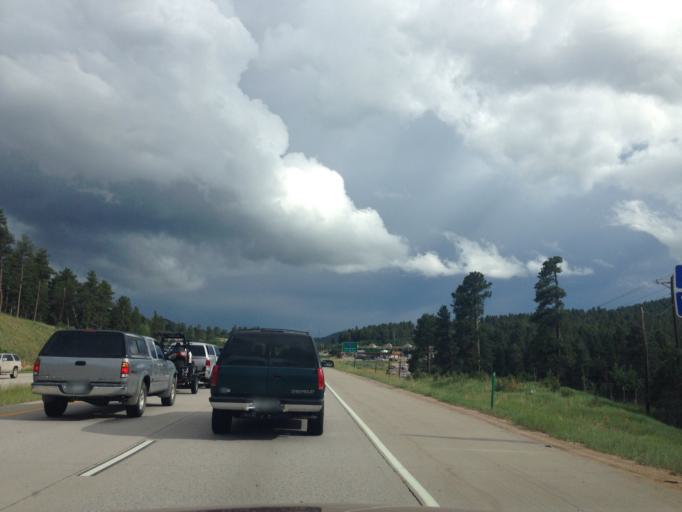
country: US
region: Colorado
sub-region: Jefferson County
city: Evergreen
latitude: 39.5243
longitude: -105.3068
